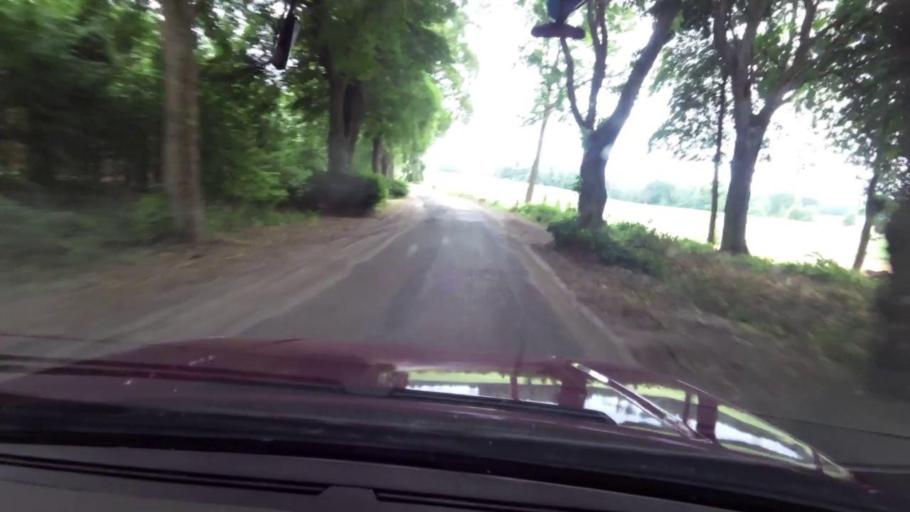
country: PL
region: Pomeranian Voivodeship
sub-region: Powiat slupski
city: Kepice
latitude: 54.1911
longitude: 16.7969
